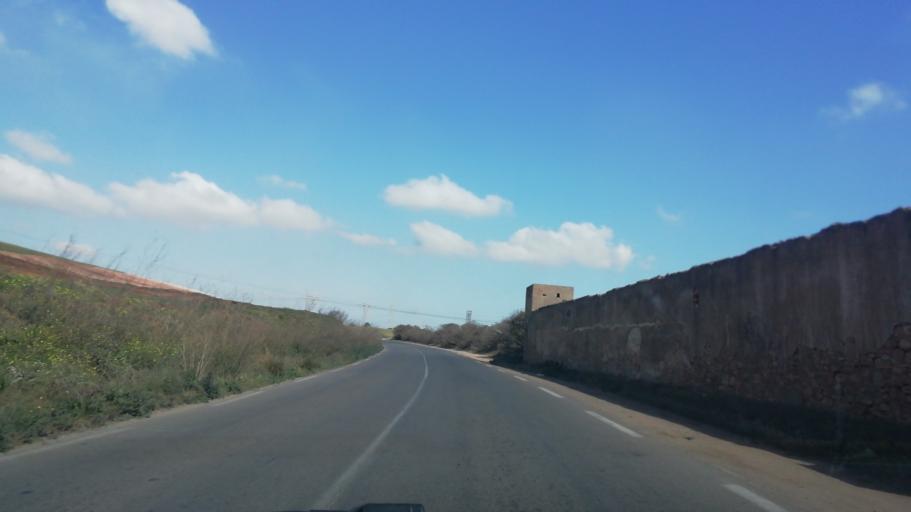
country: DZ
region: Oran
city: Ain el Bya
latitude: 35.7471
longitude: -0.2608
